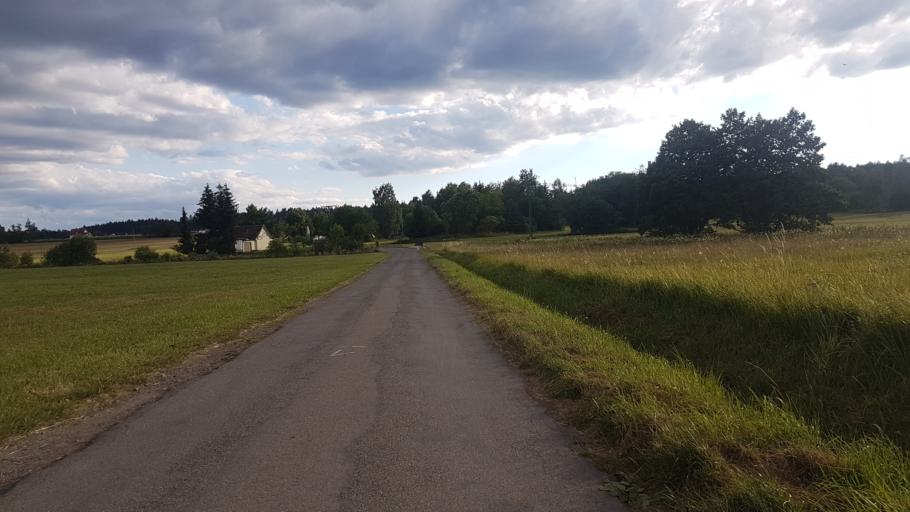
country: DE
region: Baden-Wuerttemberg
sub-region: Freiburg Region
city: Braunlingen
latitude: 47.9780
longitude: 8.4284
